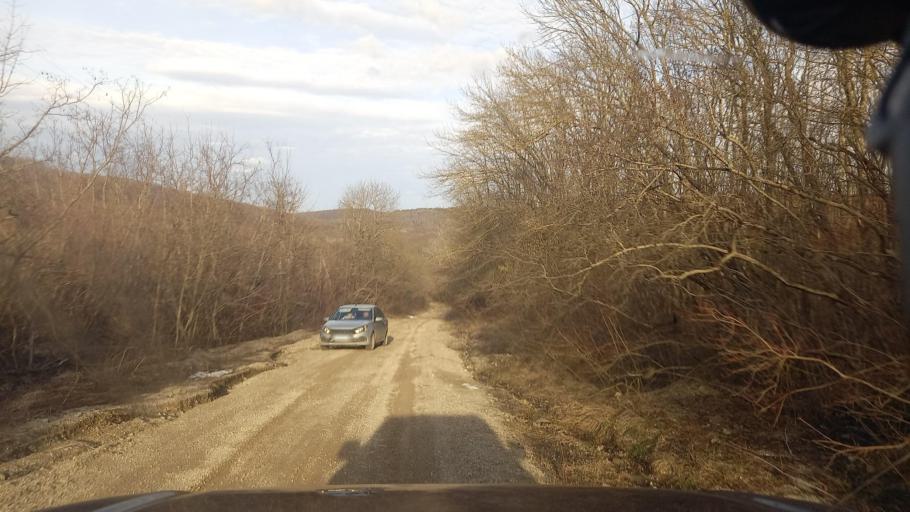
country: RU
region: Krasnodarskiy
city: Novodmitriyevskaya
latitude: 44.6969
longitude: 38.9635
